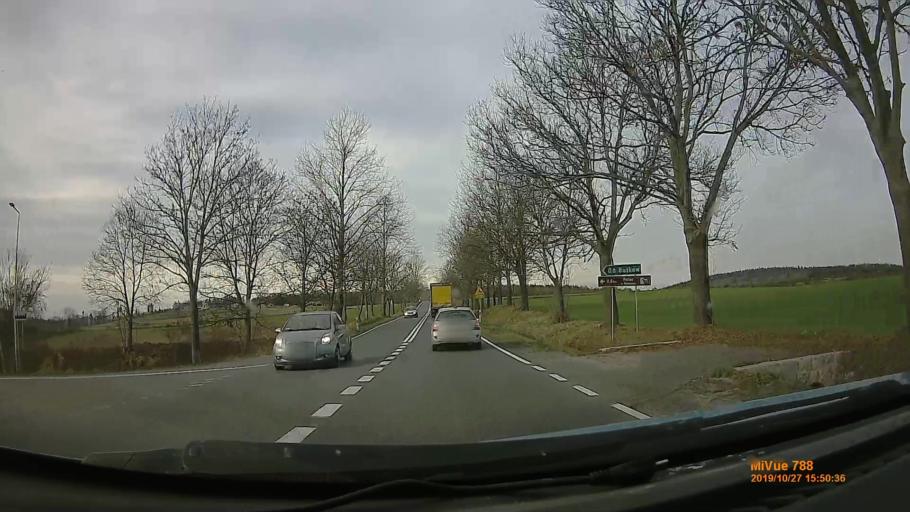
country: PL
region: Lower Silesian Voivodeship
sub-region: Powiat klodzki
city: Bozkow
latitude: 50.5188
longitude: 16.5849
